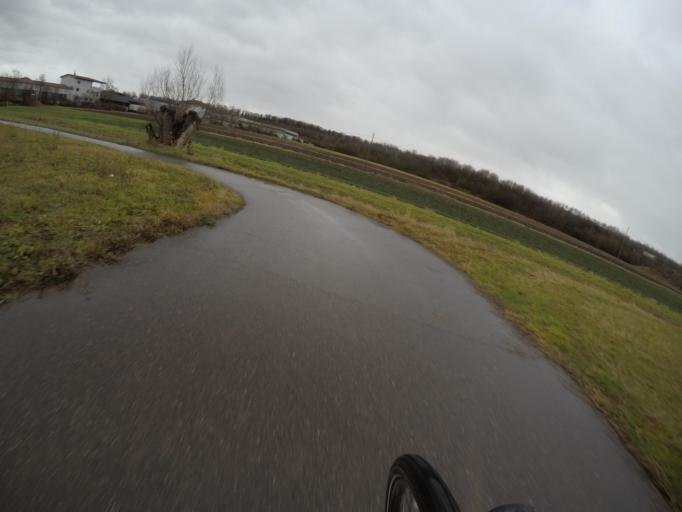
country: DE
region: Baden-Wuerttemberg
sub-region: Regierungsbezirk Stuttgart
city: Sersheim
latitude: 48.9573
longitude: 8.9991
